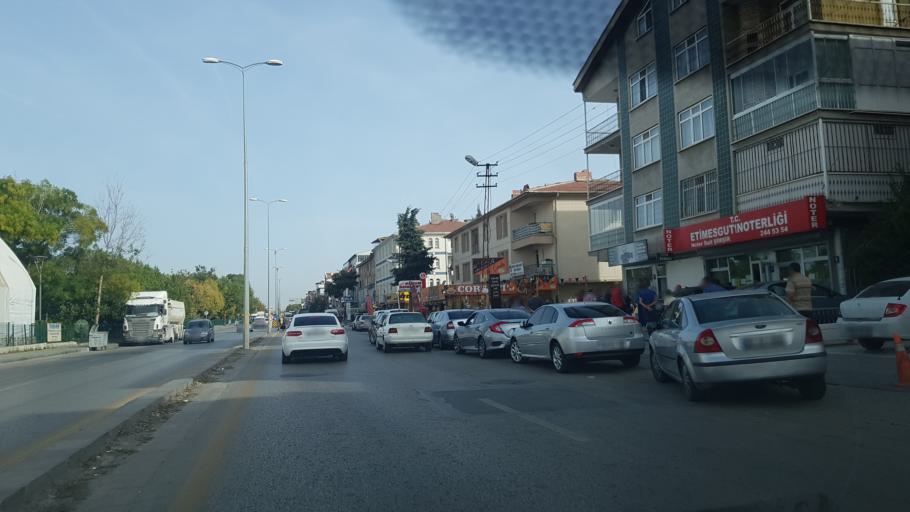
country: TR
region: Ankara
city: Etimesgut
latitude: 39.9497
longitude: 32.6575
